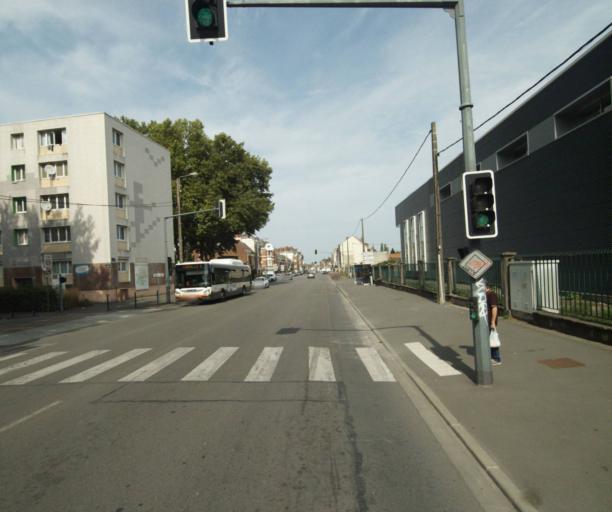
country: FR
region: Nord-Pas-de-Calais
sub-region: Departement du Nord
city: Wattignies
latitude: 50.6032
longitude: 3.0561
